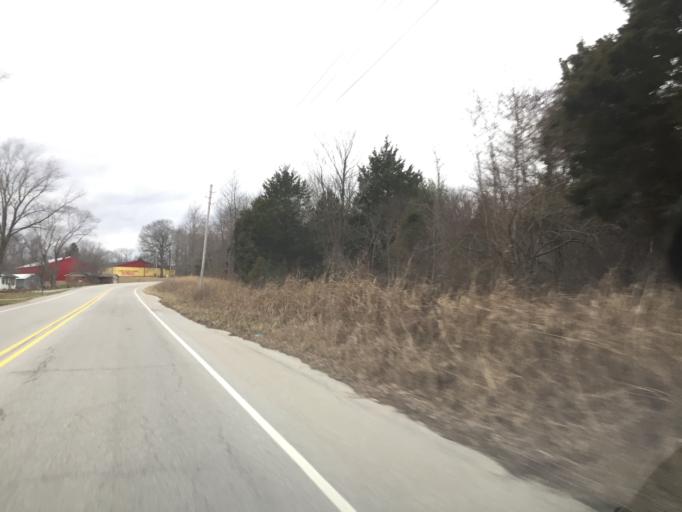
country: US
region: Indiana
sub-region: Monroe County
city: Bloomington
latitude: 39.2037
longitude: -86.5672
